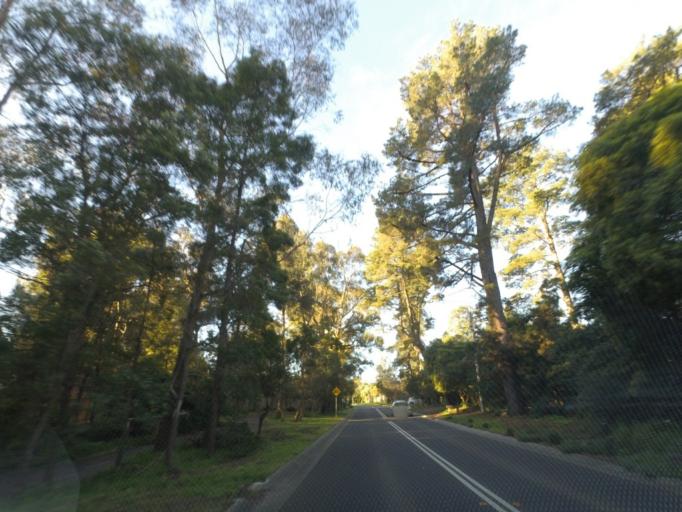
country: AU
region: Victoria
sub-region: Manningham
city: Park Orchards
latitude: -37.7827
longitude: 145.2091
